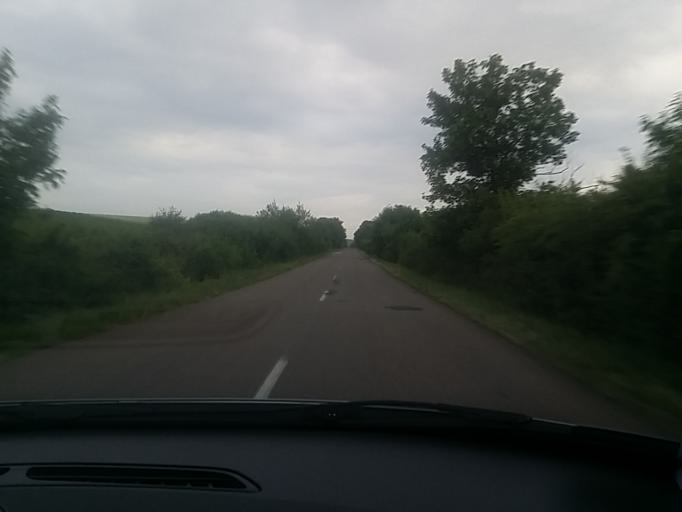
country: HU
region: Nograd
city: Paszto
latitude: 47.9079
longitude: 19.6638
